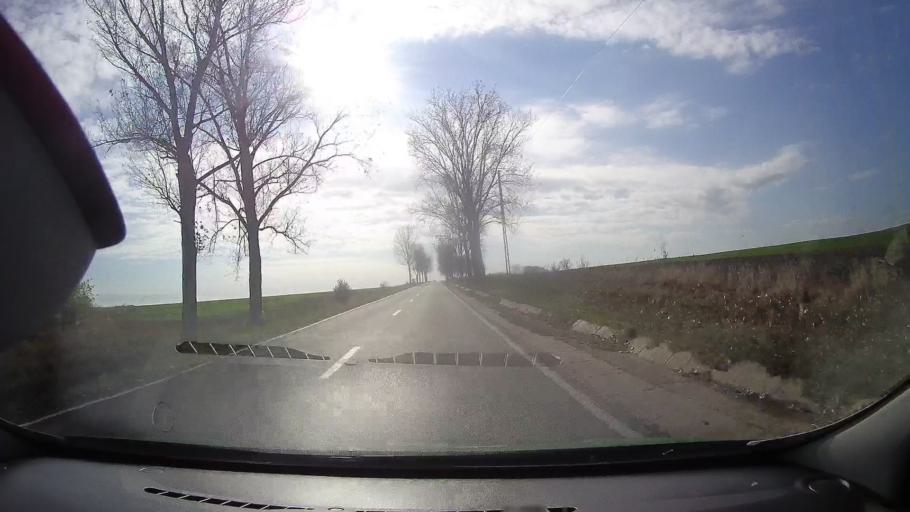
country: RO
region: Tulcea
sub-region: Comuna Valea Nucarilor
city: Agighiol
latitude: 44.9997
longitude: 28.8861
